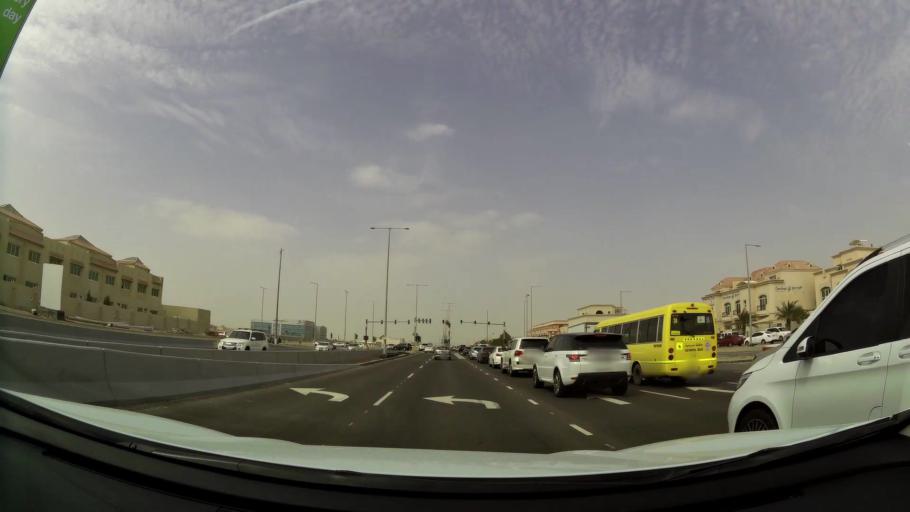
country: AE
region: Abu Dhabi
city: Abu Dhabi
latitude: 24.4028
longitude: 54.5724
